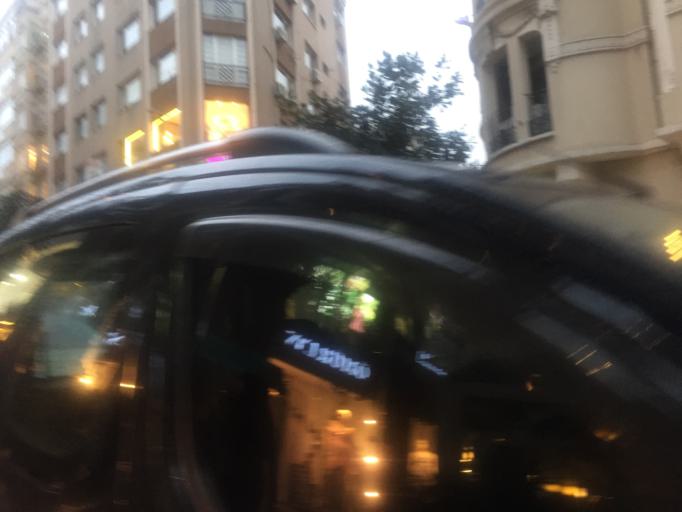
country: TR
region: Istanbul
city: Sisli
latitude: 41.0535
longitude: 28.9880
